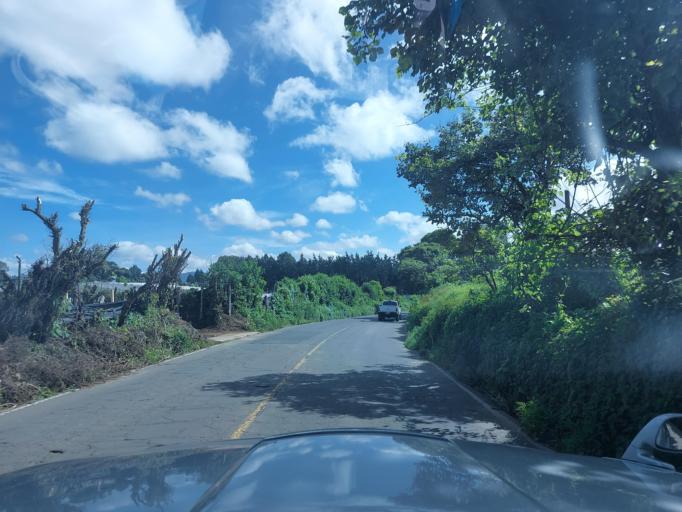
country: GT
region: Chimaltenango
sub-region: Municipio de Zaragoza
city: Zaragoza
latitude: 14.6681
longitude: -90.9007
